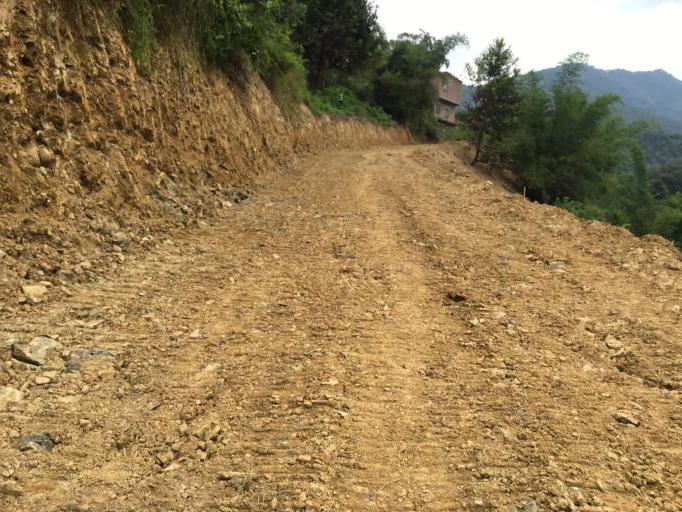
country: CN
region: Guangxi Zhuangzu Zizhiqu
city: Tongle
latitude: 25.1213
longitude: 106.4233
